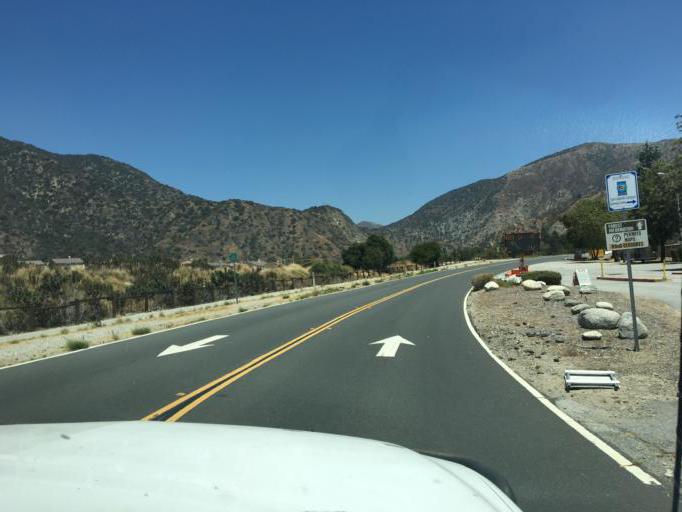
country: US
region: California
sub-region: Los Angeles County
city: Azusa
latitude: 34.1594
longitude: -117.9095
